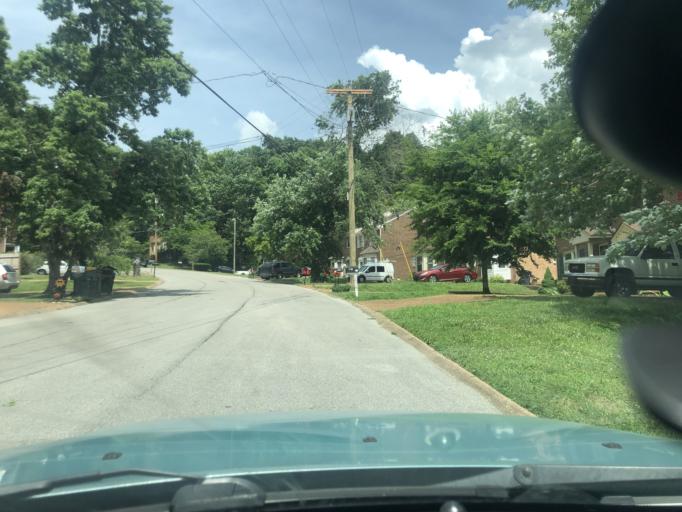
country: US
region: Tennessee
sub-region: Davidson County
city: Lakewood
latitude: 36.1285
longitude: -86.6357
